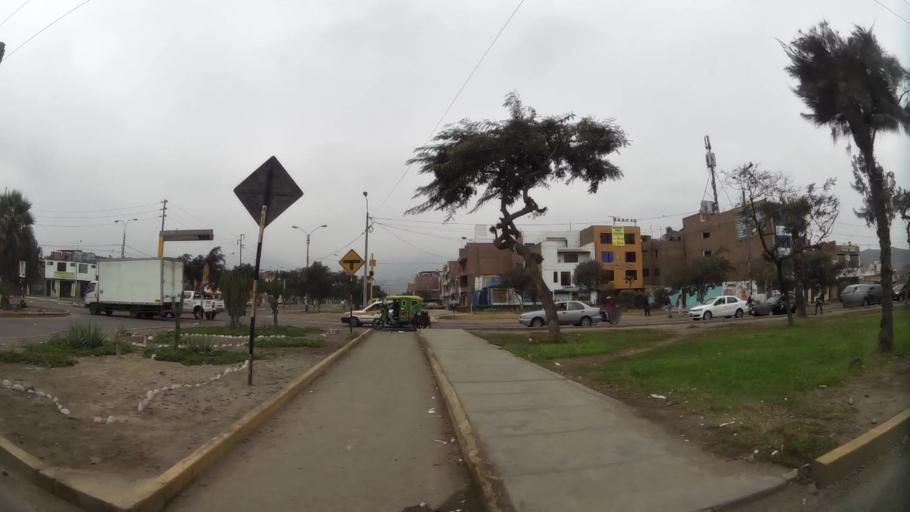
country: PE
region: Lima
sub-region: Lima
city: Independencia
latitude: -11.9835
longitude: -77.0785
